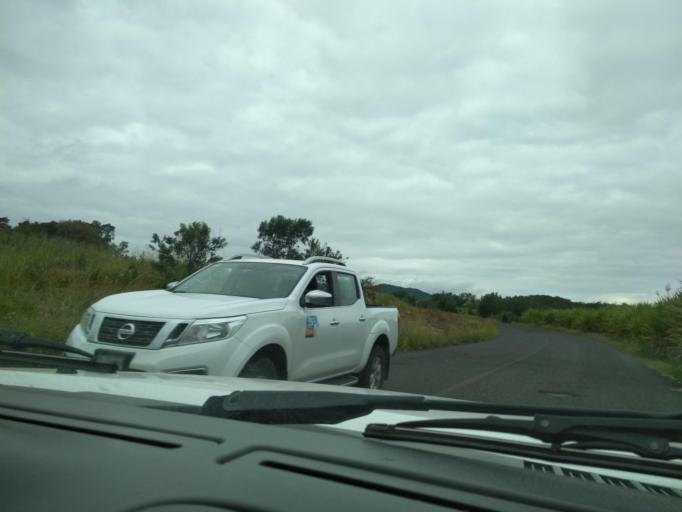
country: MX
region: Veracruz
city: El Castillo
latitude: 19.5845
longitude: -96.8122
